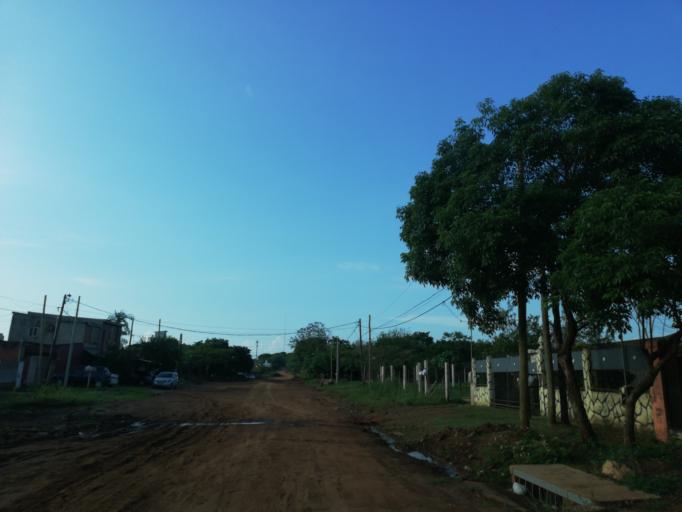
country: AR
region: Misiones
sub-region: Departamento de Capital
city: Posadas
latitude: -27.3960
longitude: -55.9244
